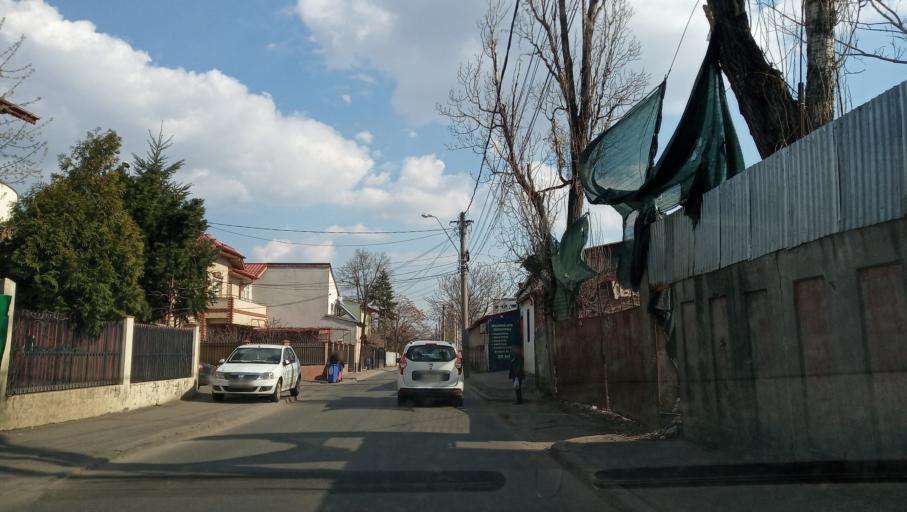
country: RO
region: Ilfov
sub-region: Comuna Fundeni-Dobroesti
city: Fundeni
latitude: 44.4539
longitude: 26.1353
